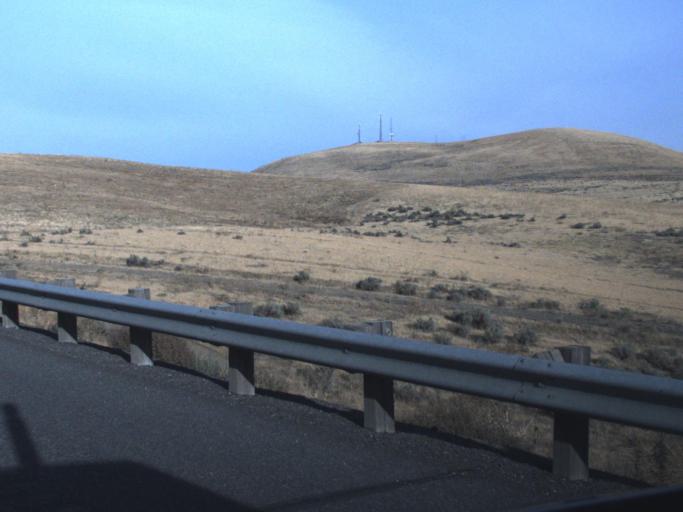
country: US
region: Oregon
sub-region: Umatilla County
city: Umatilla
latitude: 45.9803
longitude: -119.3263
